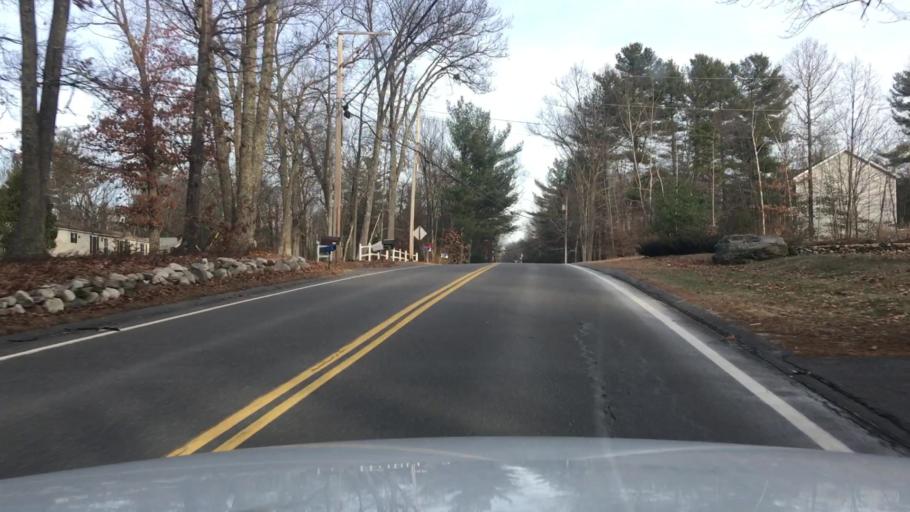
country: US
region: New Hampshire
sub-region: Rockingham County
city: Londonderry
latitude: 42.9005
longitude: -71.3828
